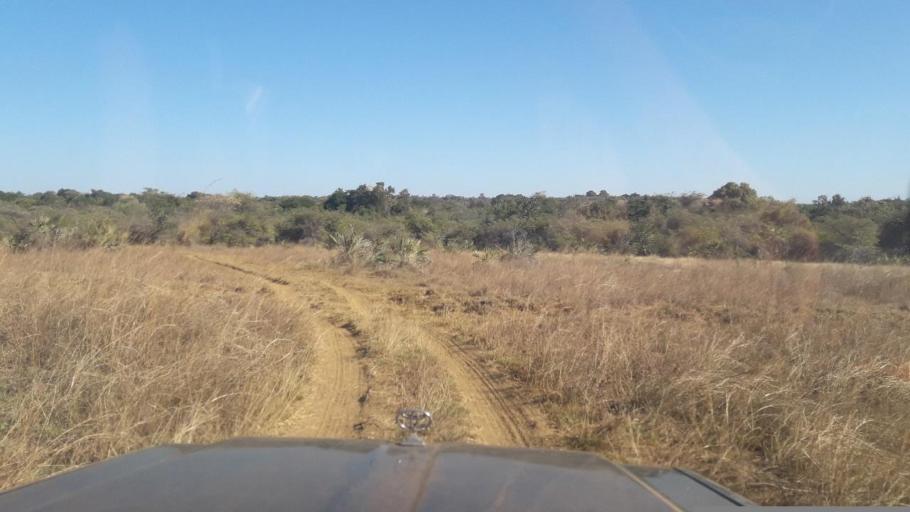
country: MG
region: Boeny
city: Sitampiky
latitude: -16.3907
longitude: 45.5923
